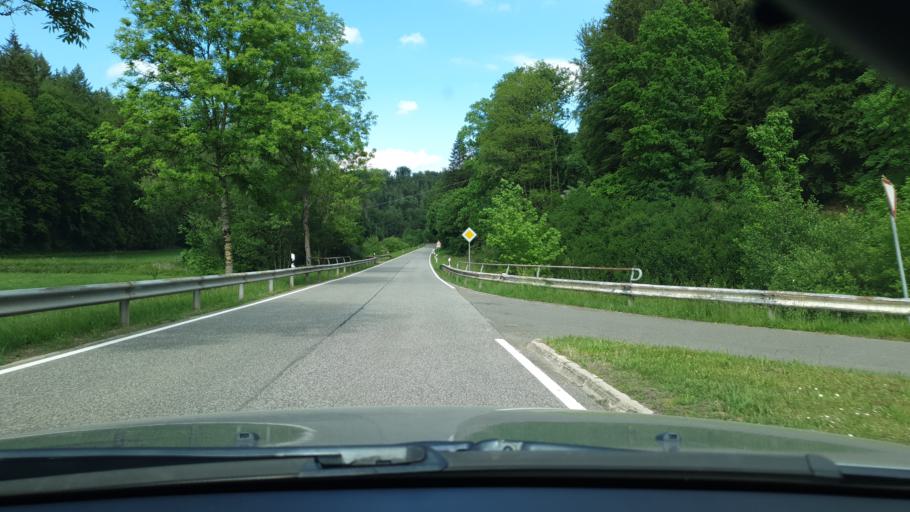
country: DE
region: Rheinland-Pfalz
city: Battweiler
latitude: 49.2796
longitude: 7.4751
